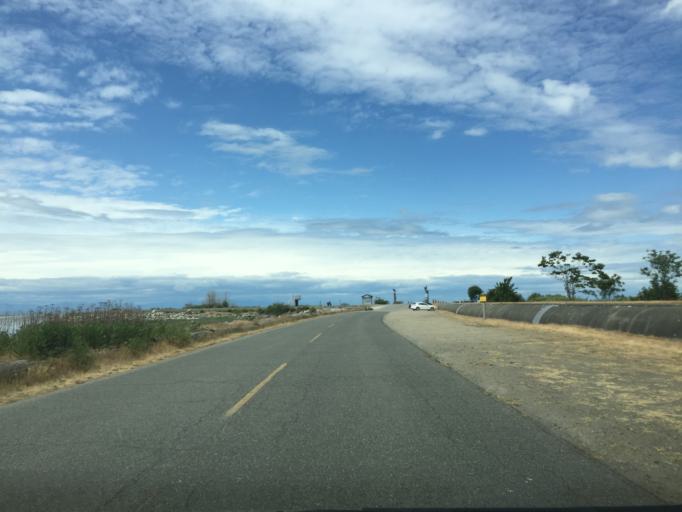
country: CA
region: British Columbia
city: Richmond
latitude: 49.2168
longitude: -123.2098
